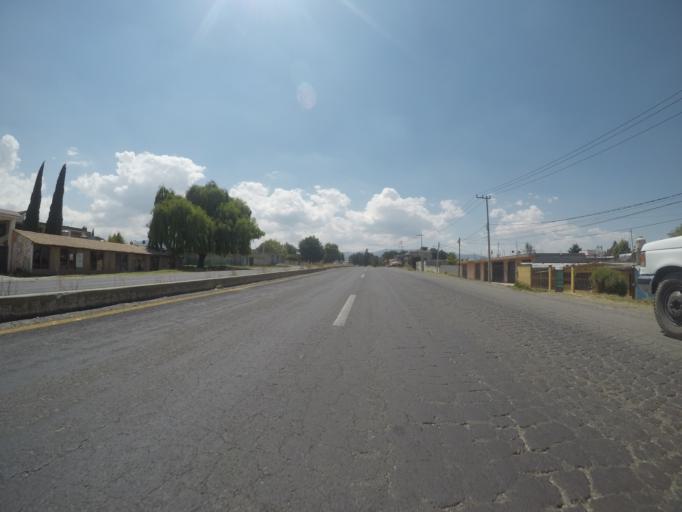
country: MX
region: Mexico
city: San Juan de las Huertas
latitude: 19.2505
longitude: -99.7601
